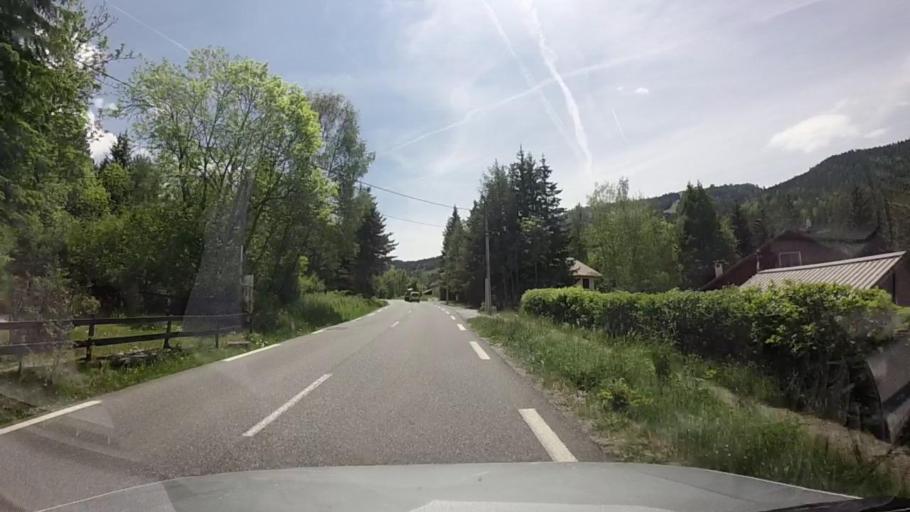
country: FR
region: Provence-Alpes-Cote d'Azur
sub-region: Departement des Alpes-de-Haute-Provence
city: Seyne-les-Alpes
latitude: 44.3308
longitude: 6.3910
